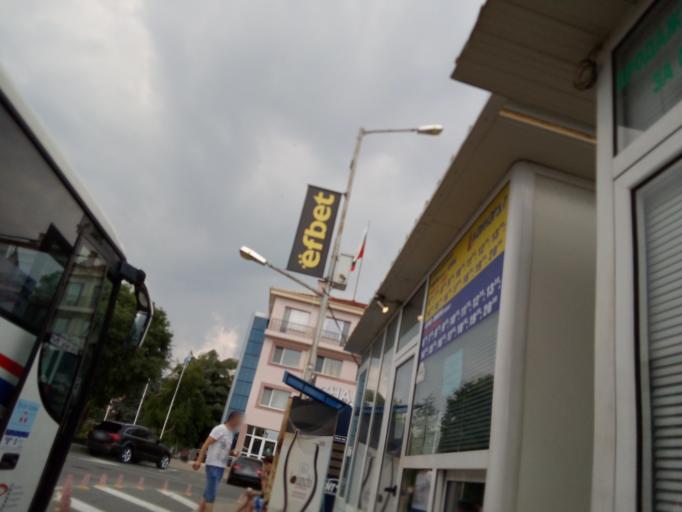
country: BG
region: Burgas
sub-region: Obshtina Pomorie
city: Pomorie
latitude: 42.5584
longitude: 27.6422
